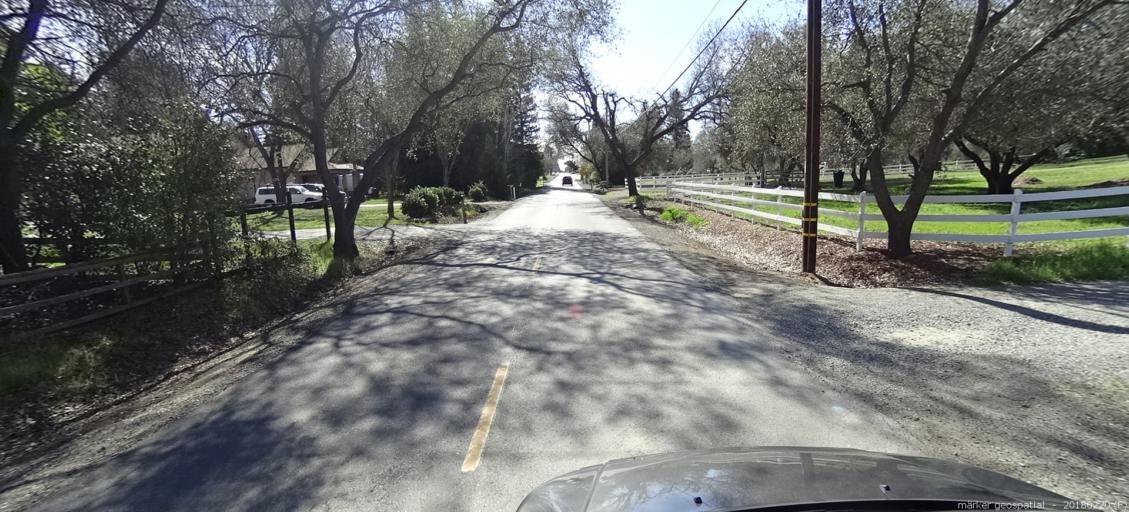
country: US
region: California
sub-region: Sacramento County
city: Orangevale
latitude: 38.6890
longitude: -121.2208
